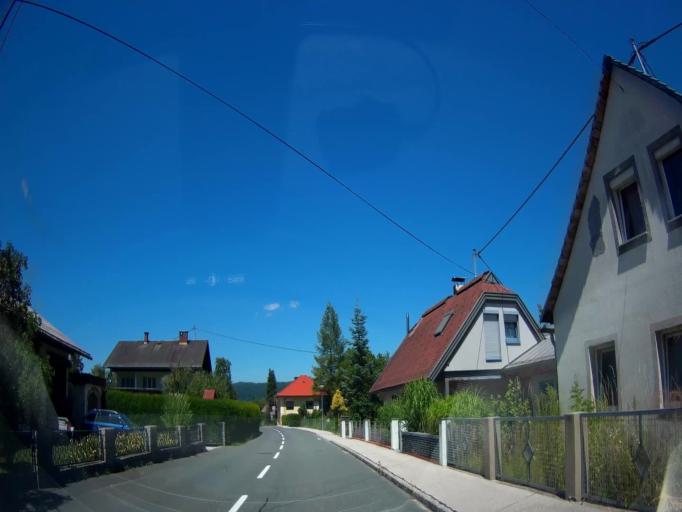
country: AT
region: Carinthia
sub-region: Politischer Bezirk Klagenfurt Land
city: Ferlach
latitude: 46.5193
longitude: 14.2975
